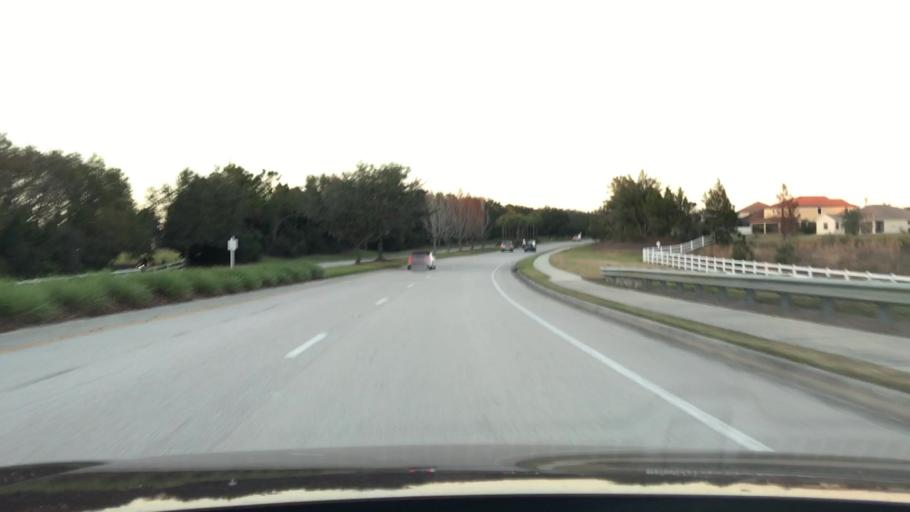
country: US
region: Florida
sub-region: Sarasota County
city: The Meadows
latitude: 27.4185
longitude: -82.3995
